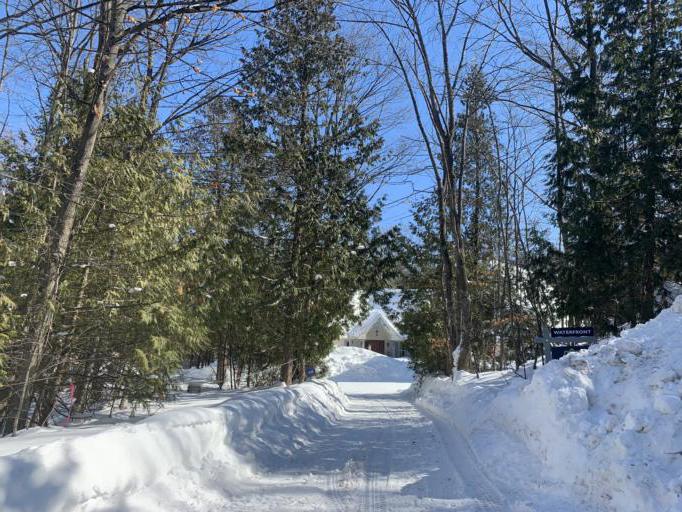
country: US
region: Wisconsin
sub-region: Door County
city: Sturgeon Bay
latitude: 45.1913
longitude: -87.1438
